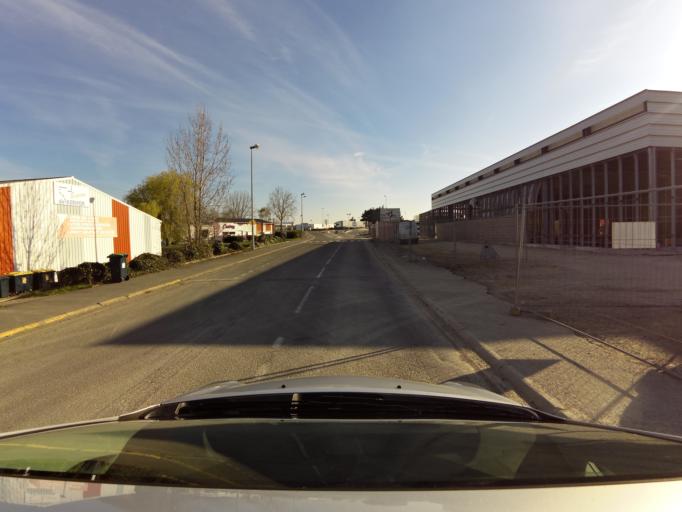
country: FR
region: Brittany
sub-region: Departement du Morbihan
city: Larmor-Plage
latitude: 47.7258
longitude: -3.3849
